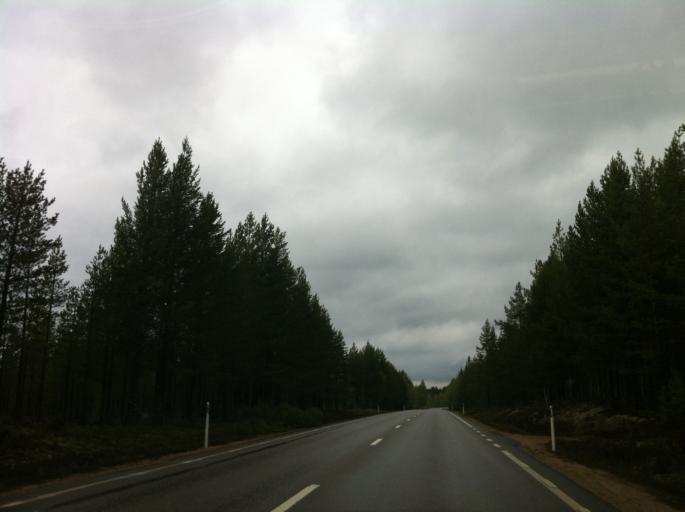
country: SE
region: Jaemtland
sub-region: Harjedalens Kommun
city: Sveg
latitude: 62.0605
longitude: 14.2878
